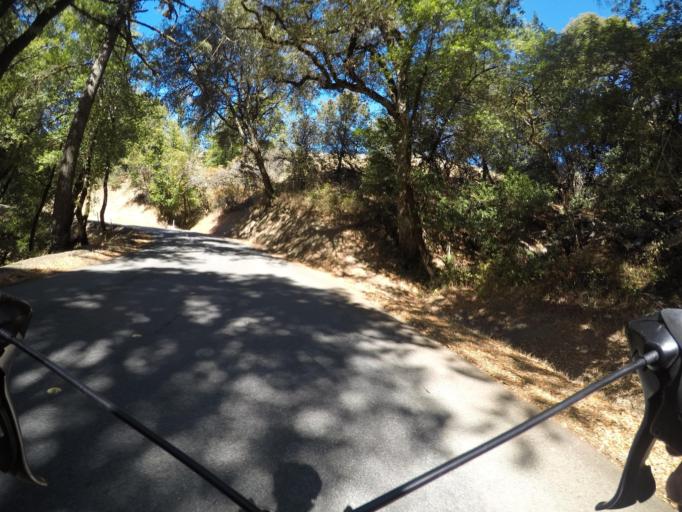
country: US
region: California
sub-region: San Mateo County
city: Portola Valley
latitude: 37.3159
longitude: -122.1924
